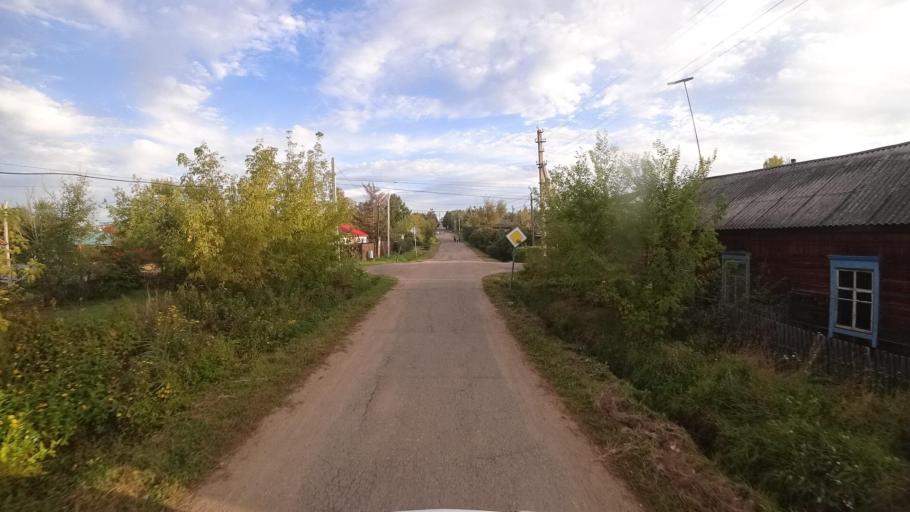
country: RU
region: Primorskiy
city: Yakovlevka
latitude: 44.4292
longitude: 133.4752
